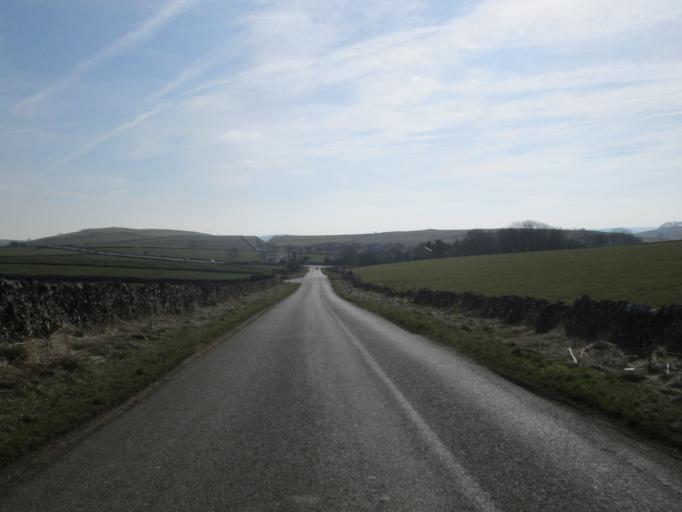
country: GB
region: England
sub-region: Derbyshire
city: Tideswell
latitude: 53.1729
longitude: -1.7789
